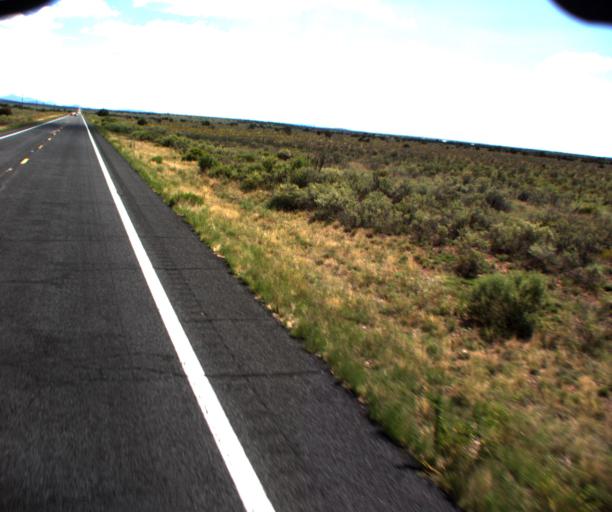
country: US
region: Arizona
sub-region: Coconino County
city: Williams
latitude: 35.5961
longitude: -112.1483
